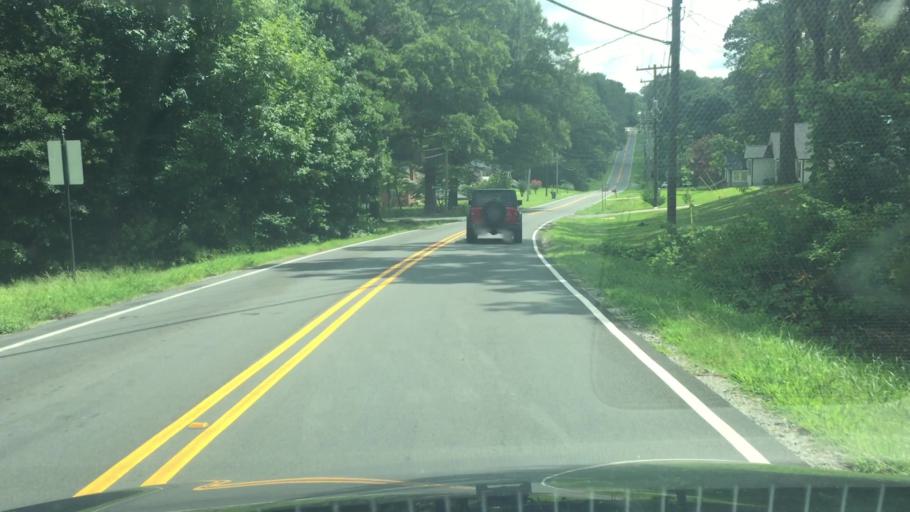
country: US
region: North Carolina
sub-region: Cabarrus County
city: Kannapolis
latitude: 35.4753
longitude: -80.6373
